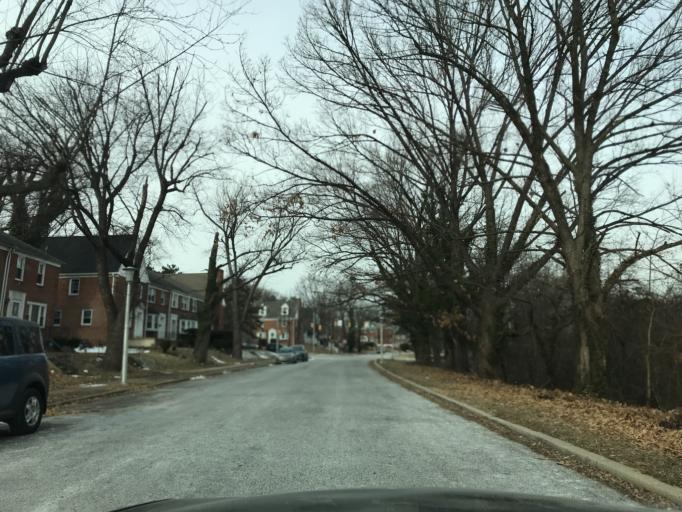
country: US
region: Maryland
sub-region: Baltimore County
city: Towson
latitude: 39.3645
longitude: -76.5992
